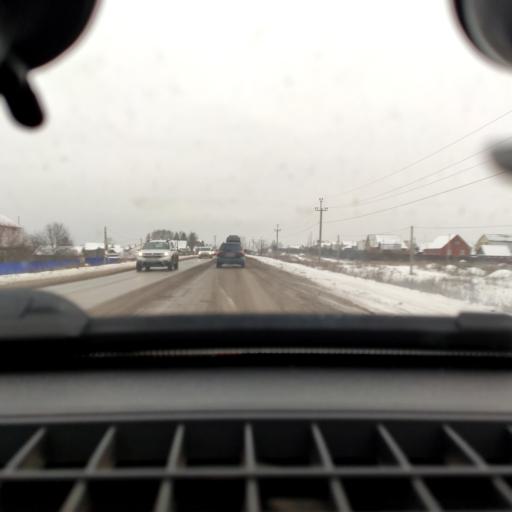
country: RU
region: Bashkortostan
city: Iglino
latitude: 54.7915
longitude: 56.2355
